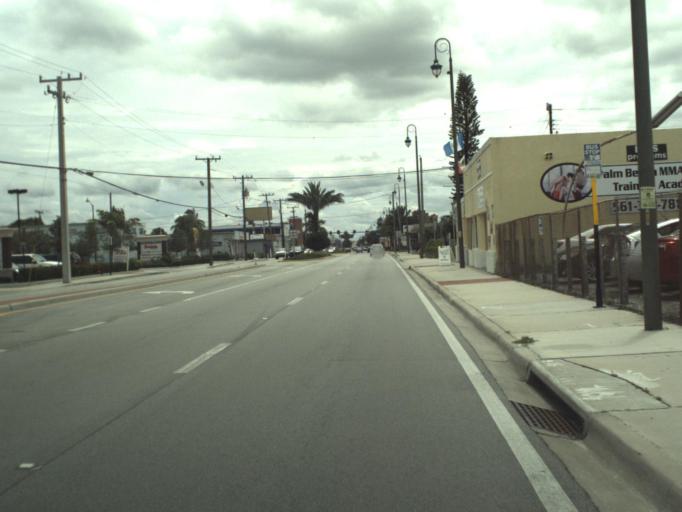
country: US
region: Florida
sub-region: Palm Beach County
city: Riviera Beach
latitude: 26.7866
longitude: -80.0548
